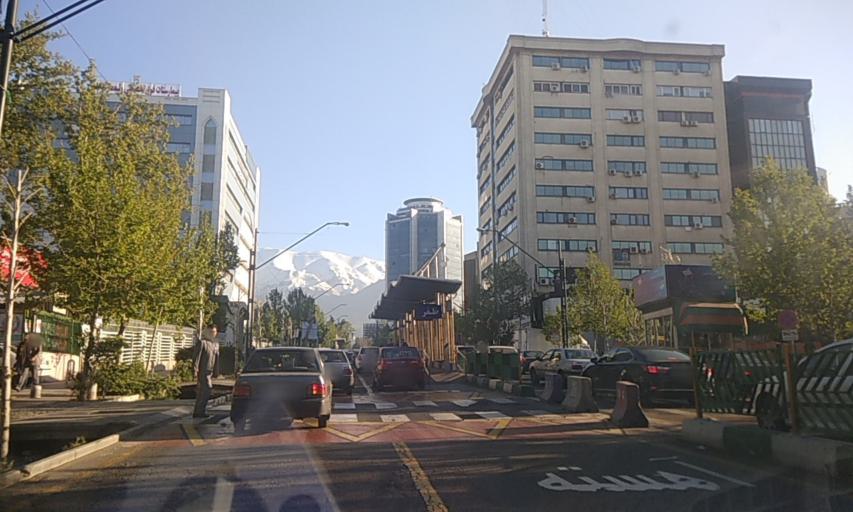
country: IR
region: Tehran
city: Tajrish
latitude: 35.7669
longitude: 51.4110
